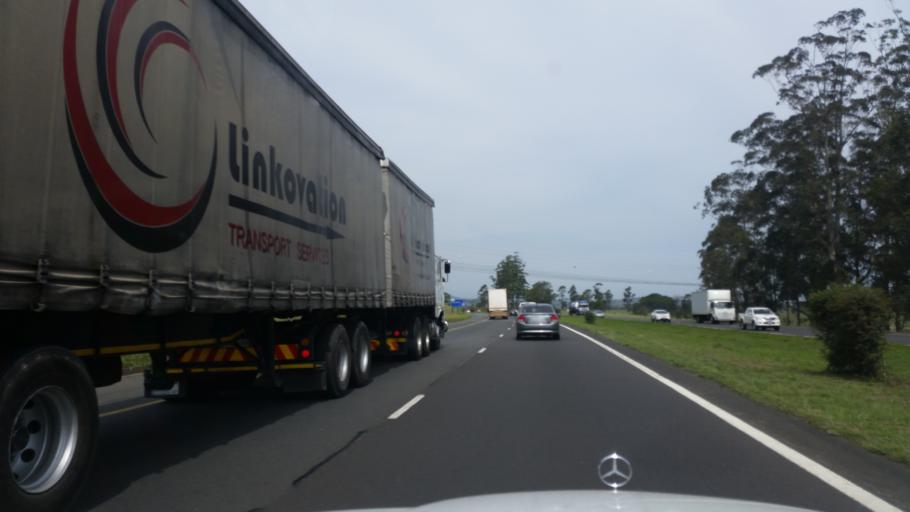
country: ZA
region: KwaZulu-Natal
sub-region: uMgungundlovu District Municipality
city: Camperdown
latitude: -29.7297
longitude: 30.5149
